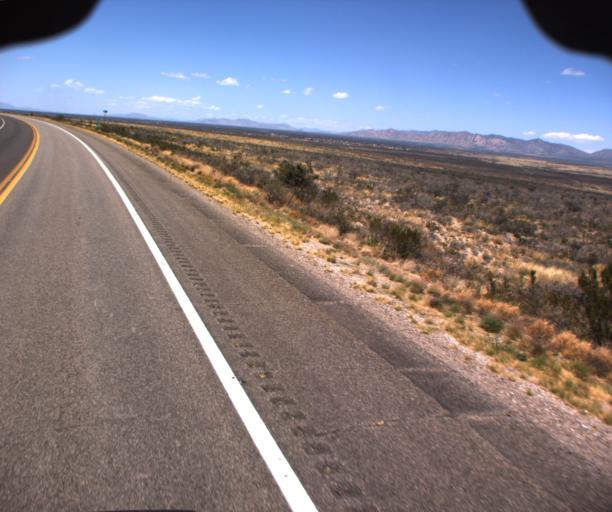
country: US
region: Arizona
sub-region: Cochise County
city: Tombstone
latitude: 31.6871
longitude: -110.0342
